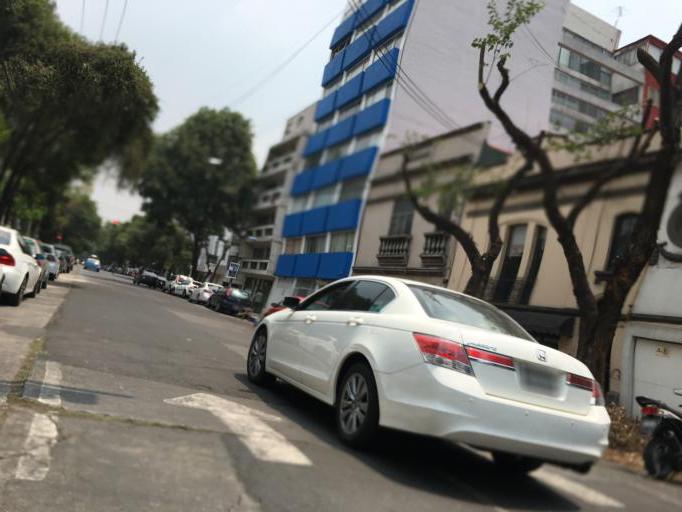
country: MX
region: Mexico City
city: Benito Juarez
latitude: 19.4156
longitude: -99.1566
